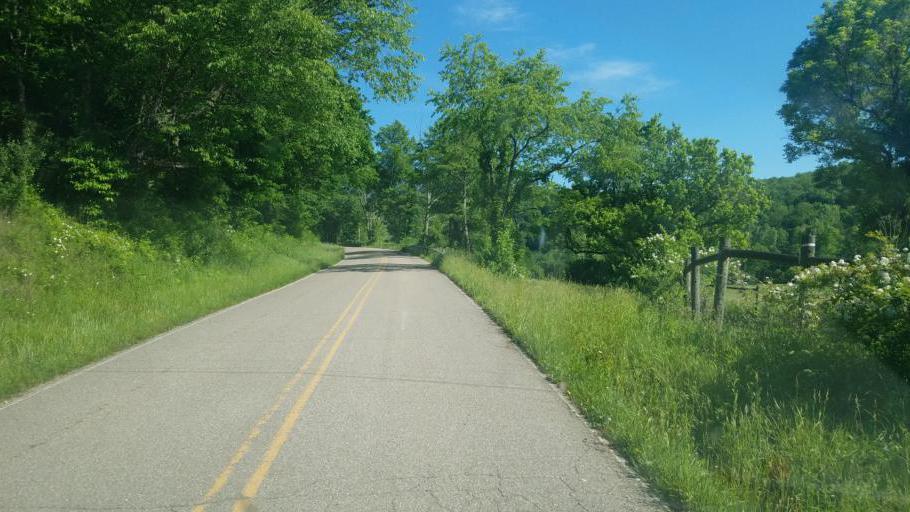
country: US
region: Ohio
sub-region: Tuscarawas County
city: Newcomerstown
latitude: 40.1807
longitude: -81.5616
